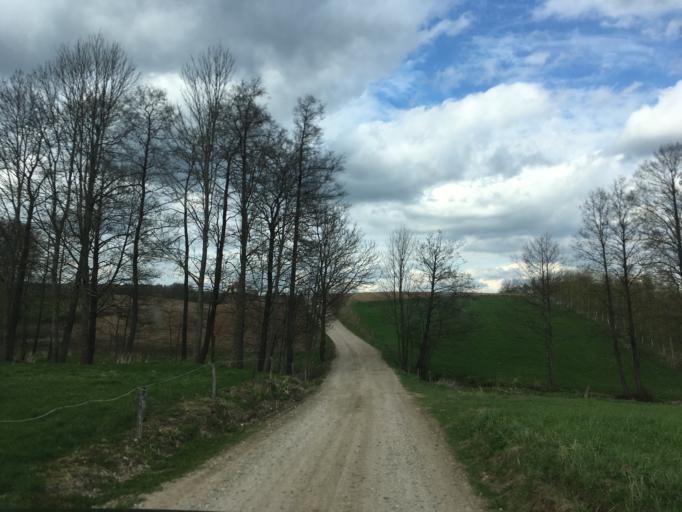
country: PL
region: Podlasie
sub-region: Powiat sejnenski
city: Punsk
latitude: 54.3788
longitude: 22.9565
